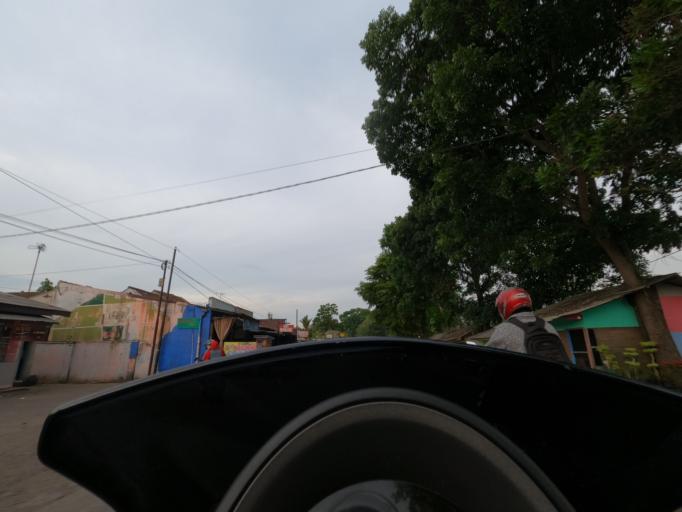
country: ID
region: West Java
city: Lembang
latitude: -6.6695
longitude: 107.7001
